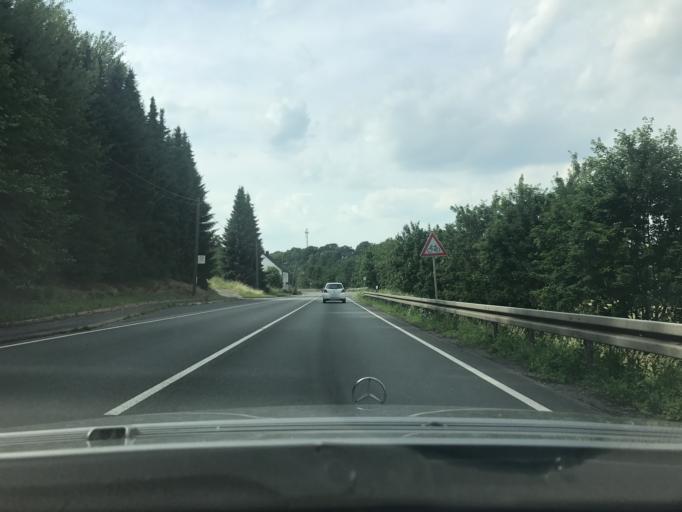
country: DE
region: North Rhine-Westphalia
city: Iserlohn
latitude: 51.4361
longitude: 7.6767
